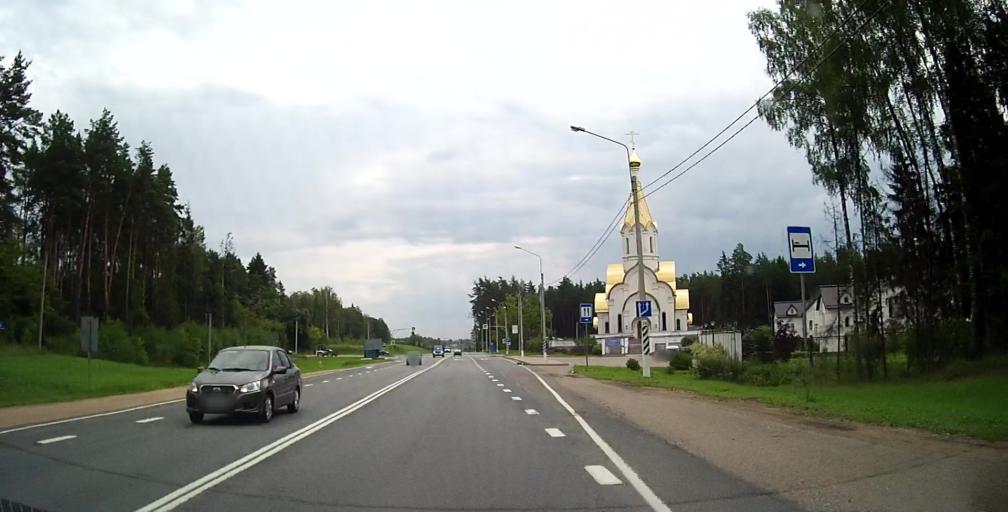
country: RU
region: Smolensk
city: Katyn'
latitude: 54.7755
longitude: 31.7856
